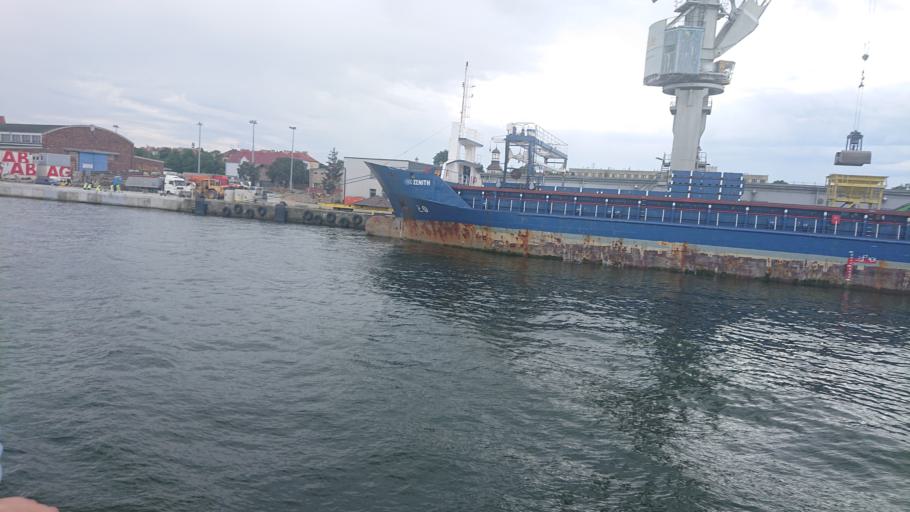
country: PL
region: Pomeranian Voivodeship
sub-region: Gdansk
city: Gdansk
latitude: 54.4043
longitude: 18.6715
